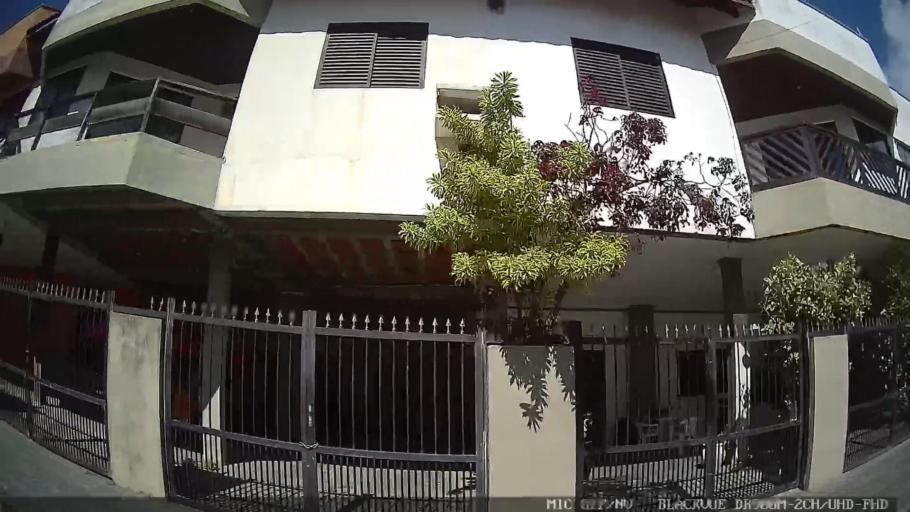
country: BR
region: Sao Paulo
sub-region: Peruibe
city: Peruibe
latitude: -24.3233
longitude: -46.9949
